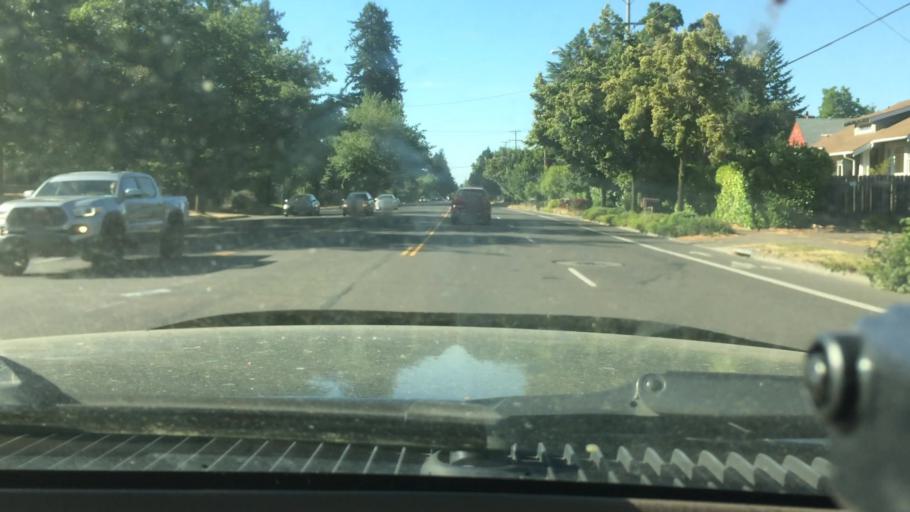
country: US
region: Oregon
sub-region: Lane County
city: Eugene
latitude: 44.0676
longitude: -123.1177
